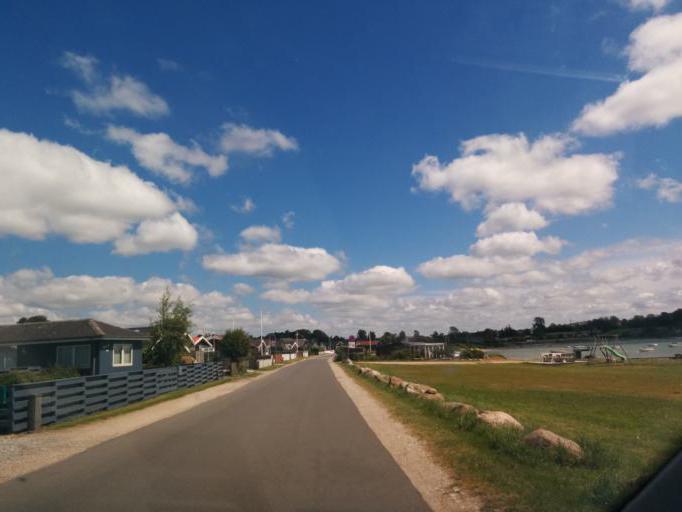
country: DK
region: Central Jutland
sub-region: Syddjurs Kommune
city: Ronde
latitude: 56.2947
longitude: 10.4247
